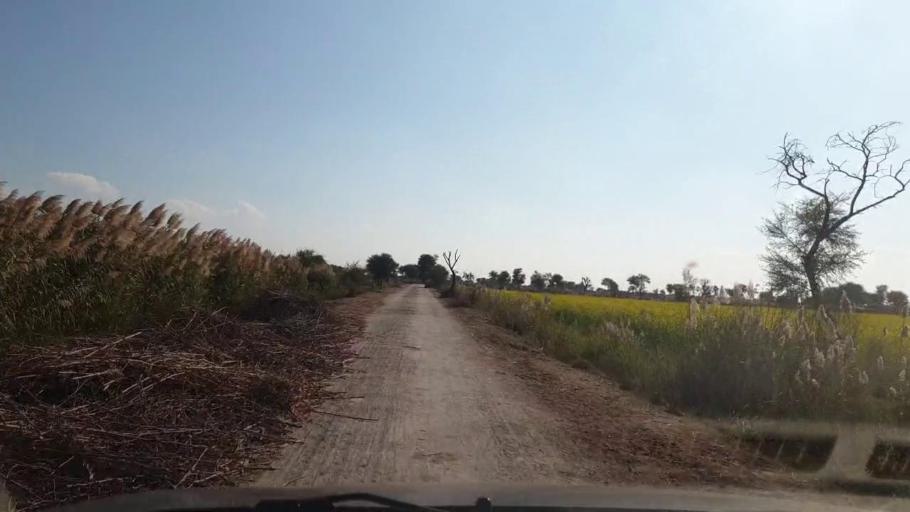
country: PK
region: Sindh
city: Sinjhoro
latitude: 25.9994
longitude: 68.7311
